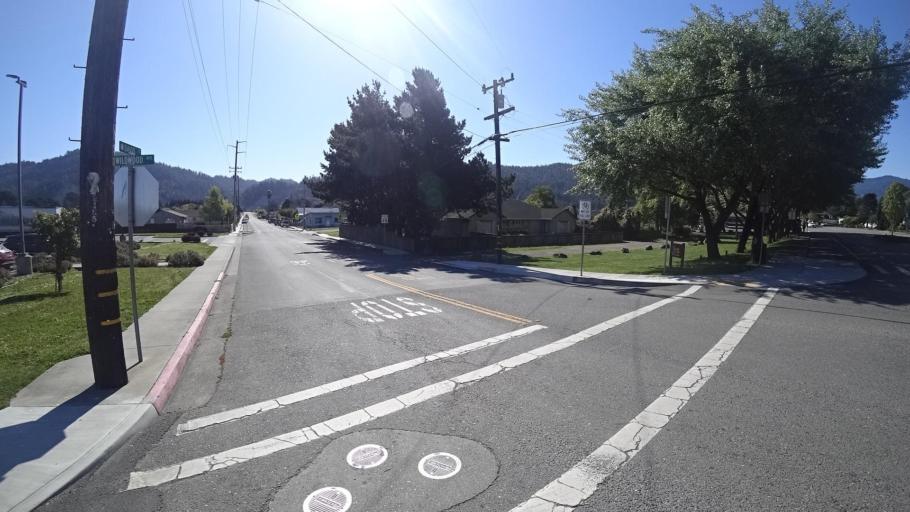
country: US
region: California
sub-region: Humboldt County
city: Rio Dell
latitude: 40.4993
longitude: -124.1060
